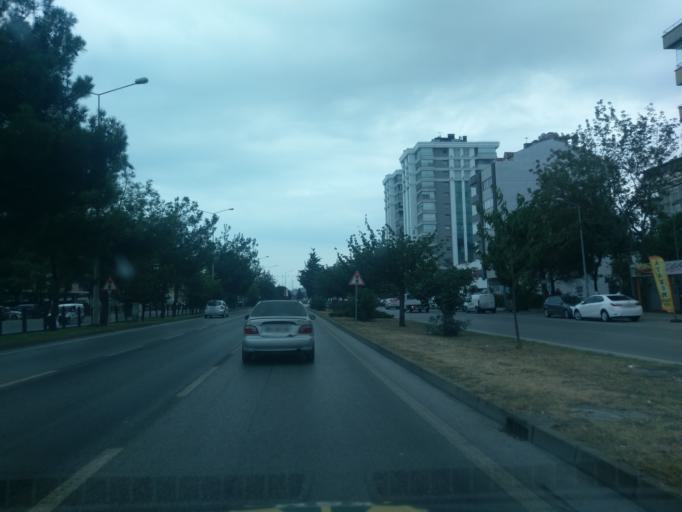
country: TR
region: Samsun
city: Samsun
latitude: 41.3337
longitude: 36.2811
